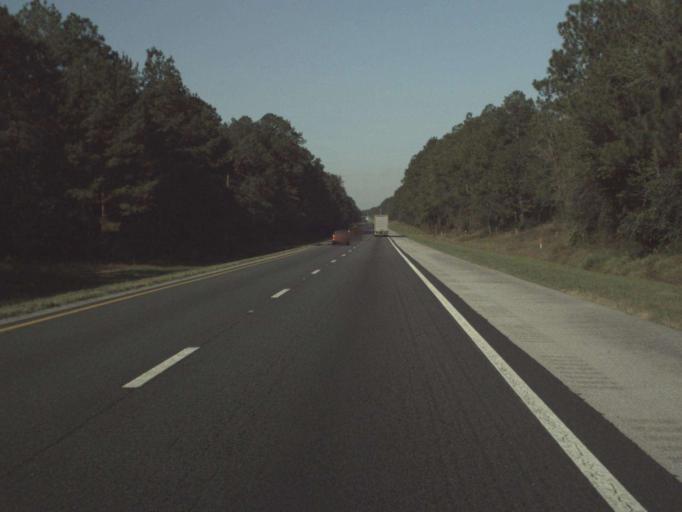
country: US
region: Florida
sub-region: Holmes County
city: Bonifay
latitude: 30.7612
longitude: -85.7627
